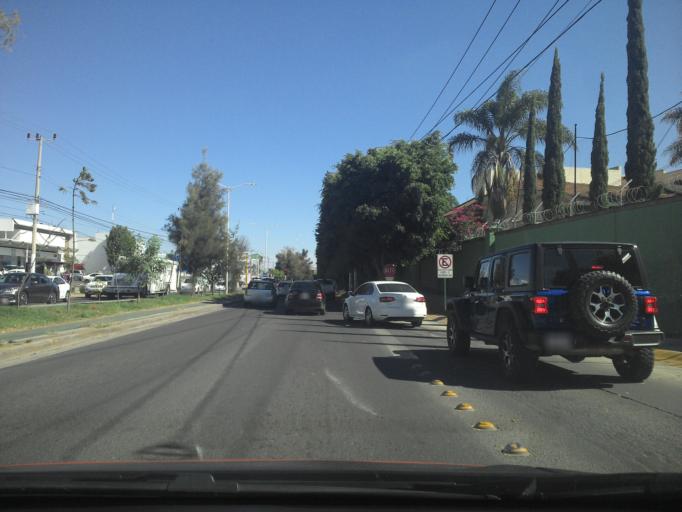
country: MX
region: Jalisco
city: Nuevo Mexico
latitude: 20.7297
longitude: -103.4396
